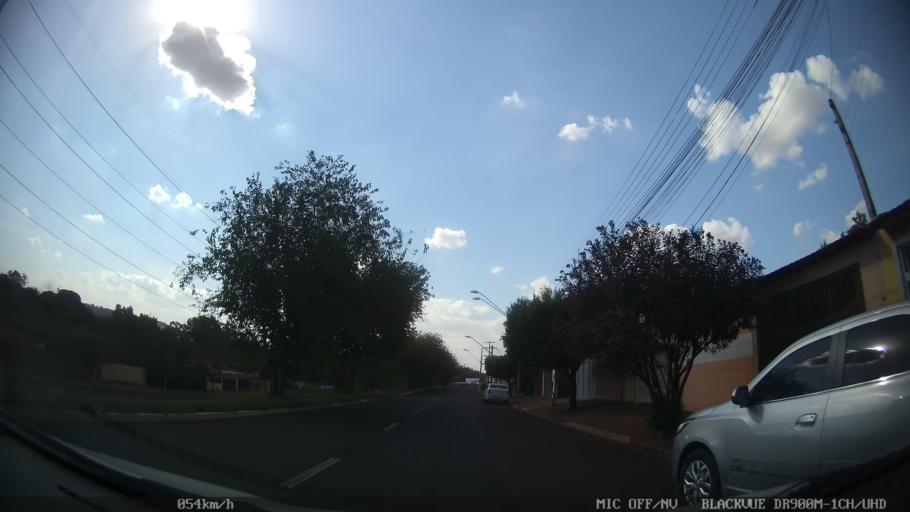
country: BR
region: Sao Paulo
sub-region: Ribeirao Preto
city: Ribeirao Preto
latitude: -21.1817
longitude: -47.8404
